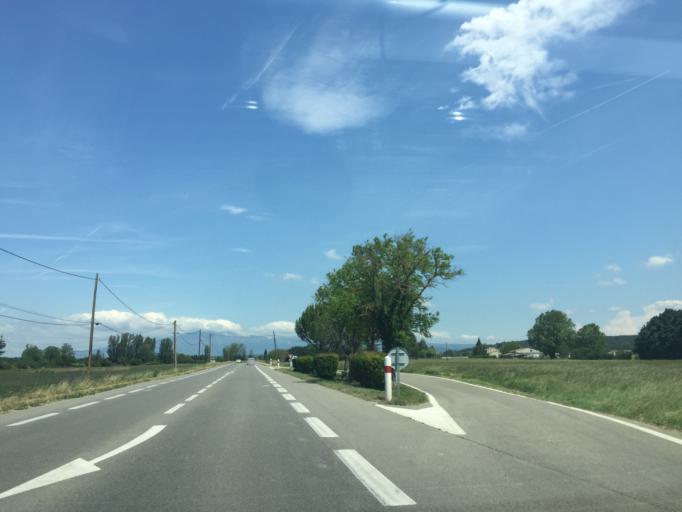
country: FR
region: Provence-Alpes-Cote d'Azur
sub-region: Departement du Vaucluse
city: Velleron
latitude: 43.9859
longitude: 5.0267
